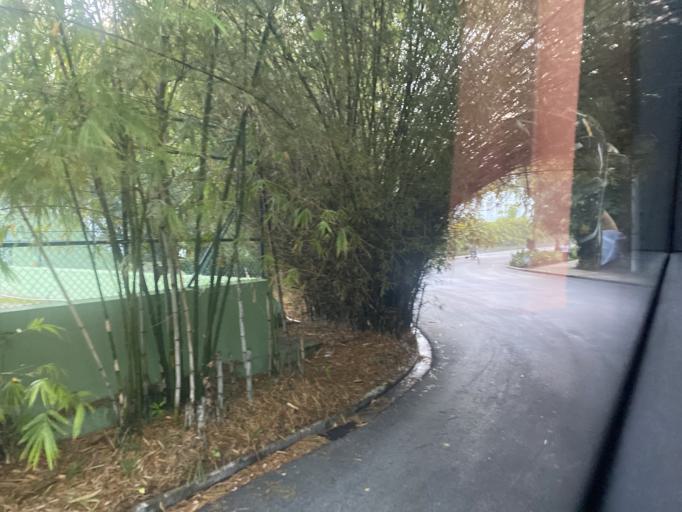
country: DO
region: San Juan
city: Punta Cana
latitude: 18.7201
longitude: -68.4578
